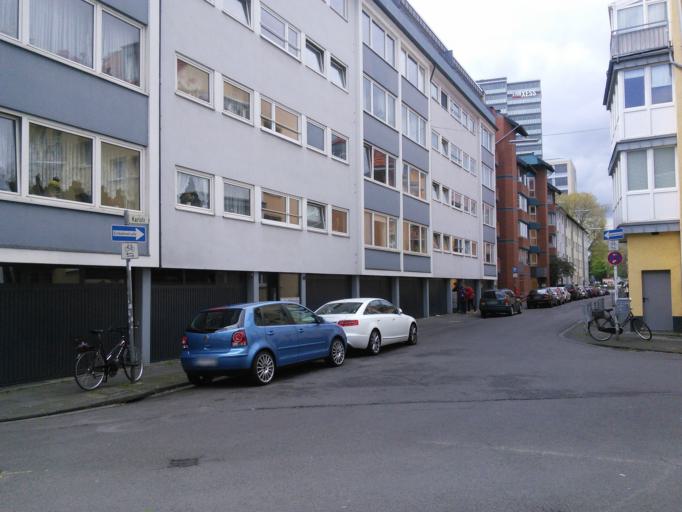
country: DE
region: North Rhine-Westphalia
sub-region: Regierungsbezirk Koln
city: Deutz
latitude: 50.9378
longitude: 6.9742
